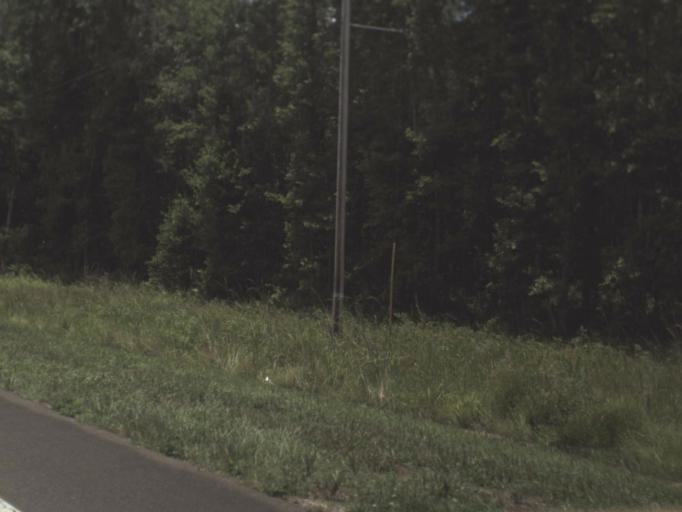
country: US
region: Florida
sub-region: Alachua County
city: Alachua
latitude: 29.7729
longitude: -82.3694
